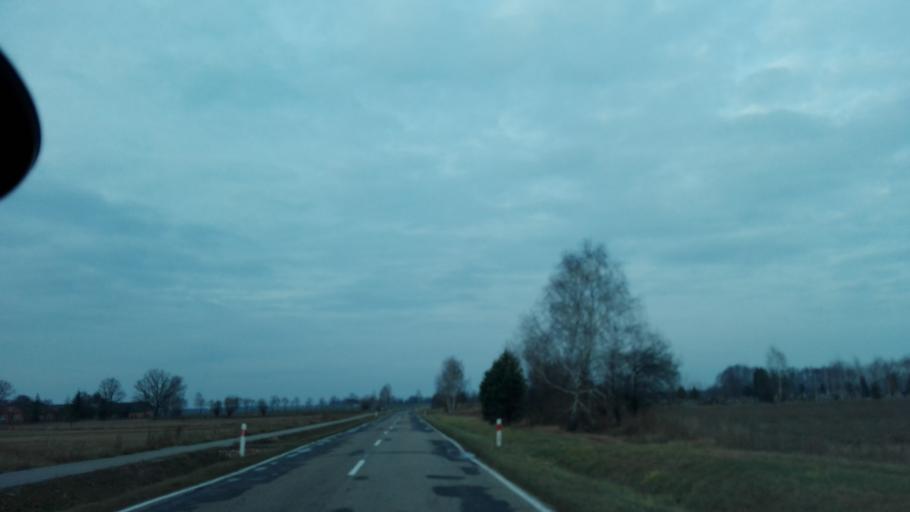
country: PL
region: Lublin Voivodeship
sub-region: Powiat bialski
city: Slawatycze
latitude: 51.6742
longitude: 23.5104
